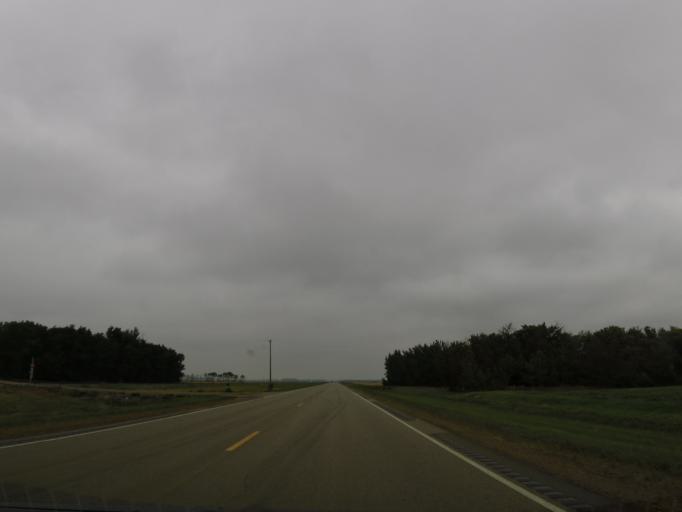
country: US
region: Minnesota
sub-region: Marshall County
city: Warren
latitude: 48.2883
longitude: -96.8038
